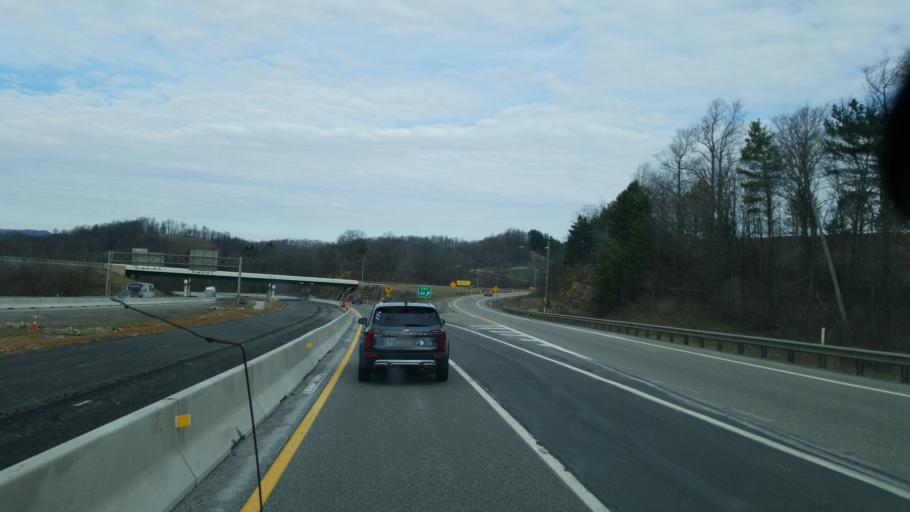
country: US
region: West Virginia
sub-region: Raleigh County
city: Prosperity
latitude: 37.8333
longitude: -81.2139
